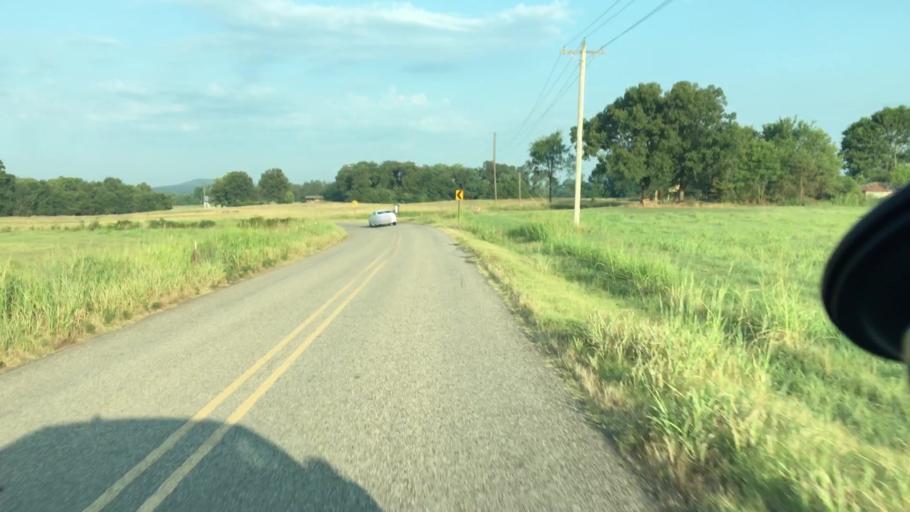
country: US
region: Arkansas
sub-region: Johnson County
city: Coal Hill
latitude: 35.3712
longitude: -93.5867
